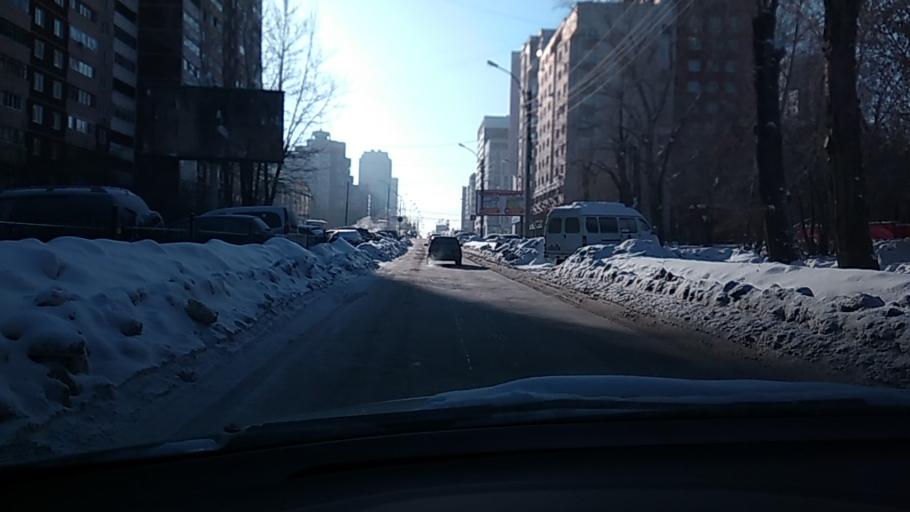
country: RU
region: Sverdlovsk
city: Yekaterinburg
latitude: 56.8093
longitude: 60.5980
